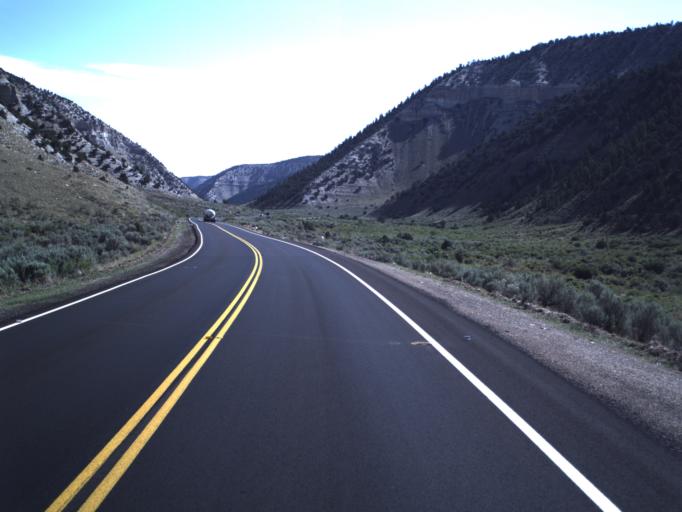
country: US
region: Utah
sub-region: Duchesne County
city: Duchesne
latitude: 39.9923
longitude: -110.5930
